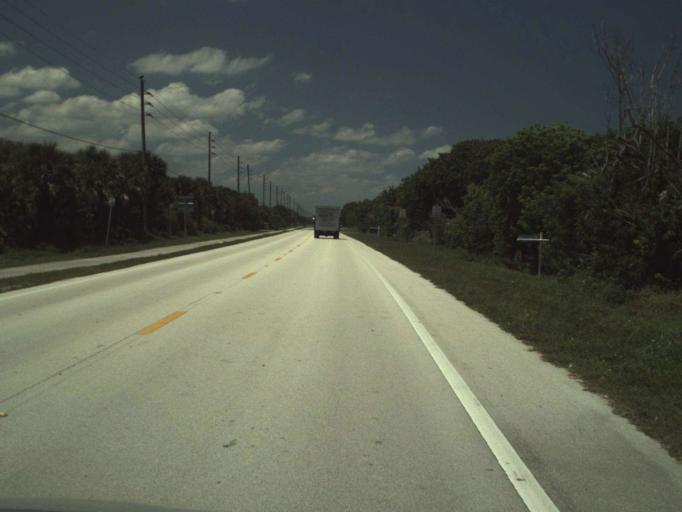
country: US
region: Florida
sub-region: Brevard County
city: Micco
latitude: 27.8913
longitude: -80.4651
